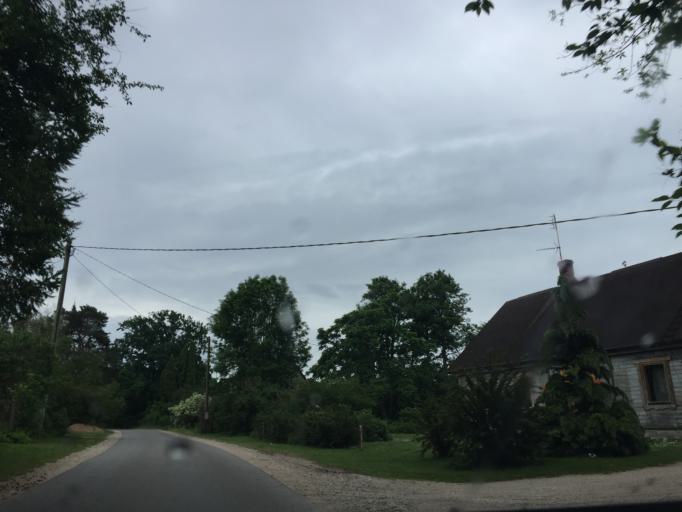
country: LV
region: Tukuma Rajons
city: Engure
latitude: 57.0792
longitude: 23.2696
